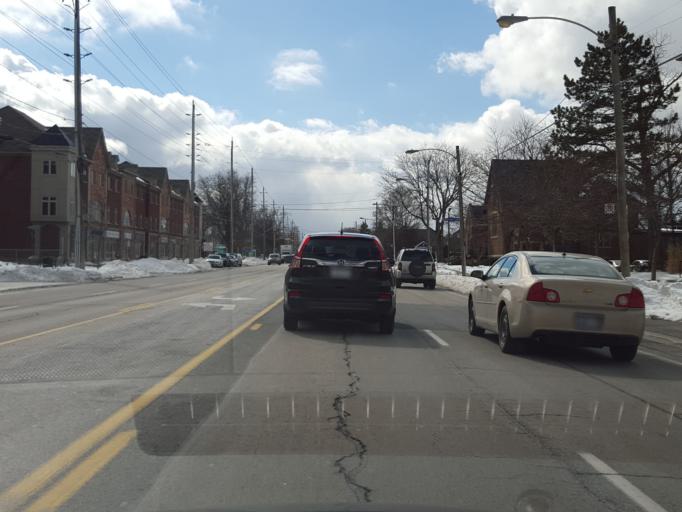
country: CA
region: Ontario
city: Hamilton
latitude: 43.3168
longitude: -79.8395
